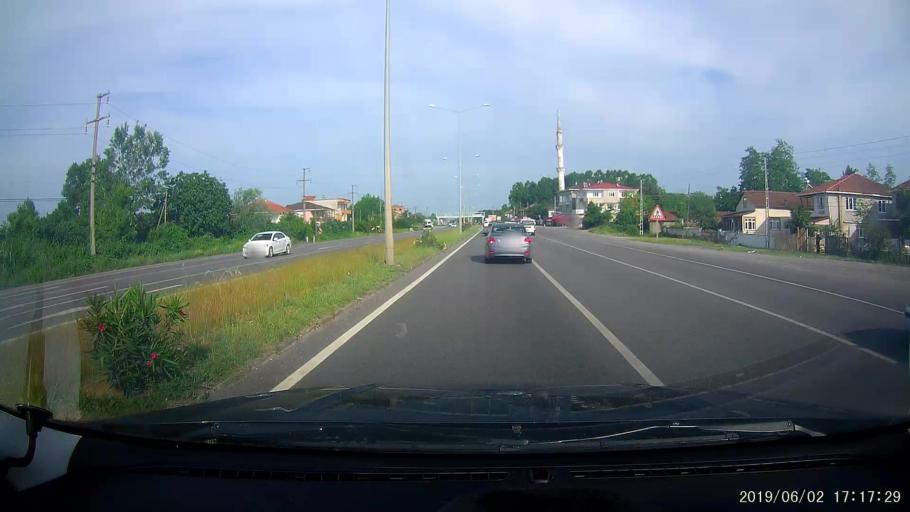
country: TR
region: Samsun
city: Dikbiyik
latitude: 41.2285
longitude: 36.5829
